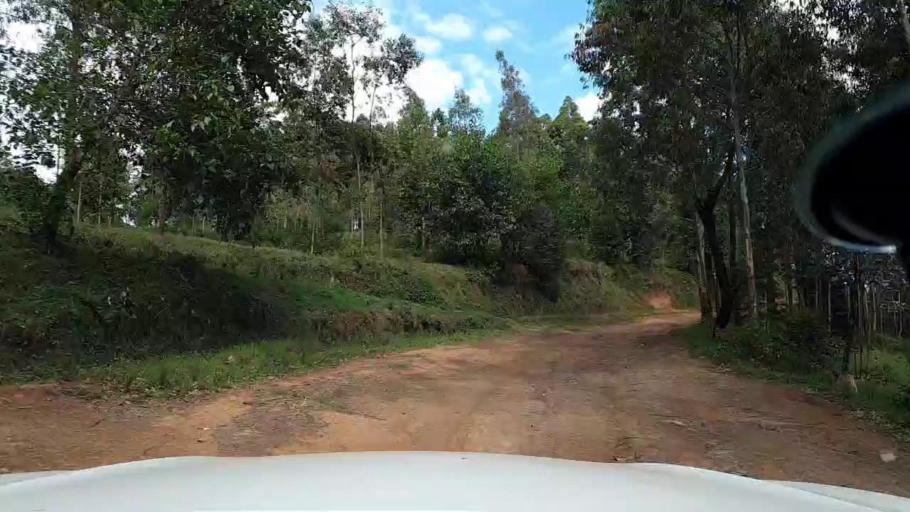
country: RW
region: Kigali
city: Kigali
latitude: -1.7881
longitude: 29.8288
